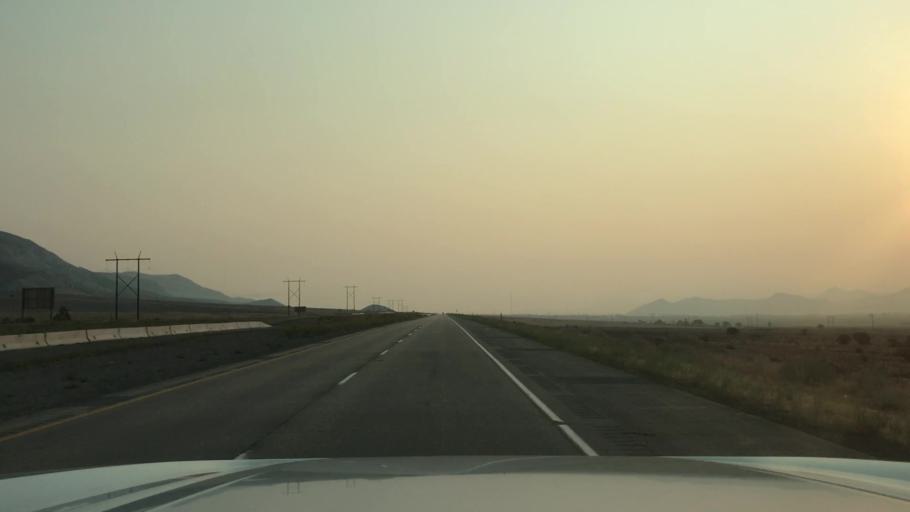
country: US
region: Utah
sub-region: Sevier County
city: Richfield
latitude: 38.8093
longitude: -112.0584
